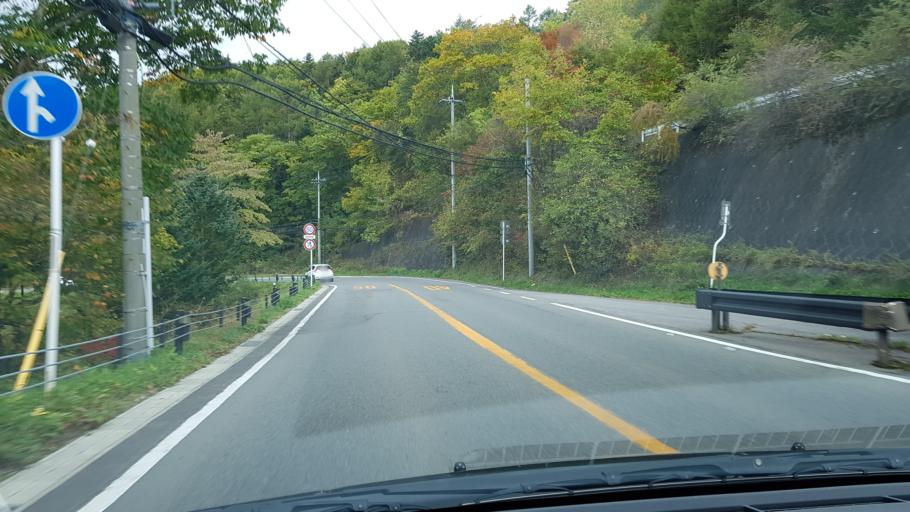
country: JP
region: Gunma
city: Nakanojomachi
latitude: 36.6076
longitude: 138.5841
